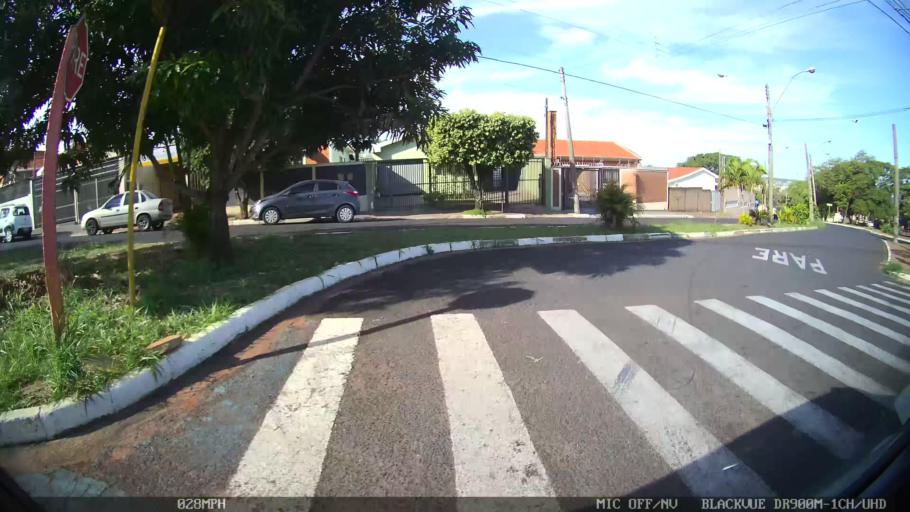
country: BR
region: Sao Paulo
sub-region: Araraquara
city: Araraquara
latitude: -21.7902
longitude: -48.1573
